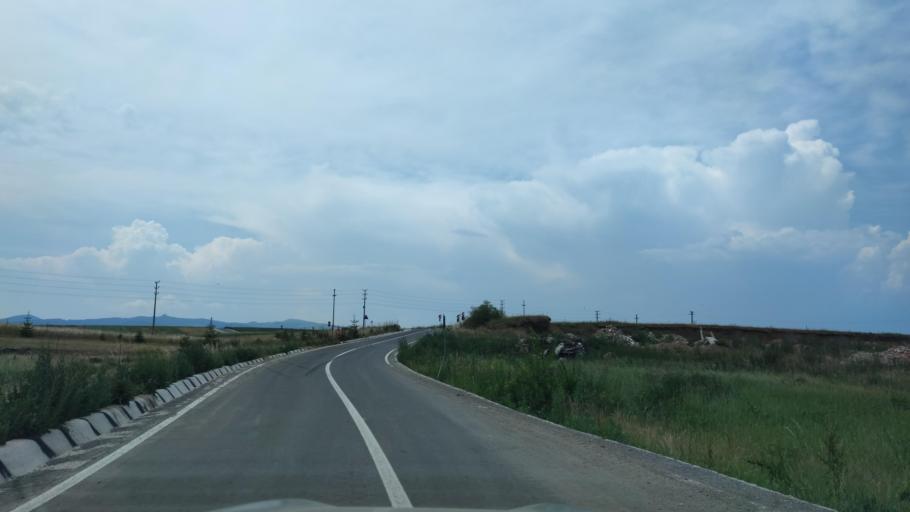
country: RO
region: Harghita
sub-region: Comuna Subcetate
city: Subcetate
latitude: 46.8178
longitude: 25.4560
